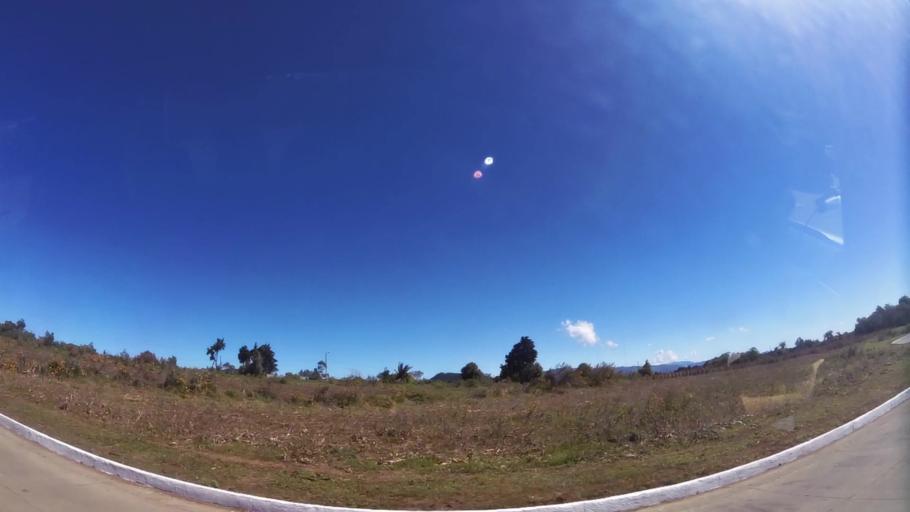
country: GT
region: Guatemala
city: San Jose Pinula
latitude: 14.5172
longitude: -90.4520
